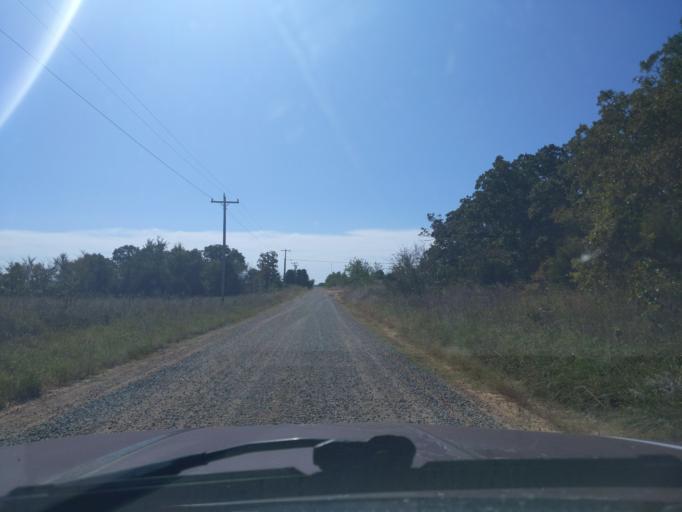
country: US
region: Oklahoma
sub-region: Okfuskee County
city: Boley
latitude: 35.6550
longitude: -96.4234
